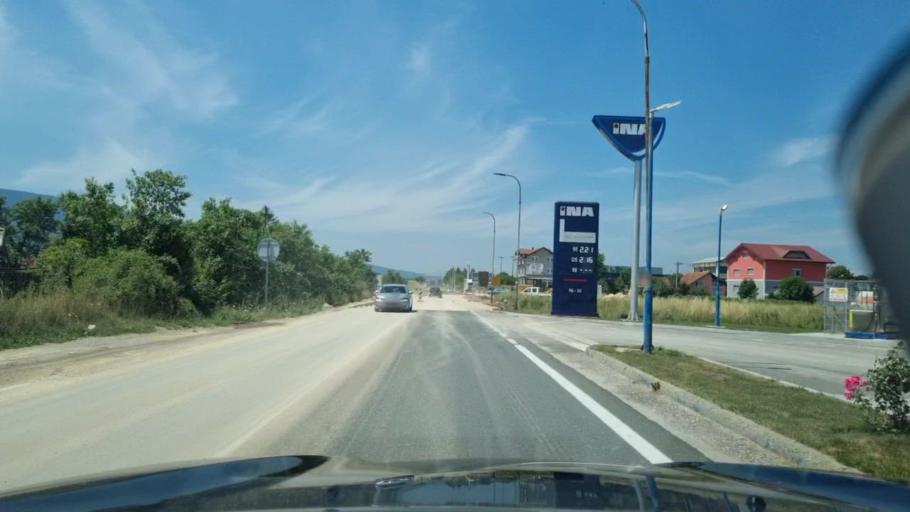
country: BA
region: Federation of Bosnia and Herzegovina
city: Sanica
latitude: 44.5446
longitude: 16.3659
